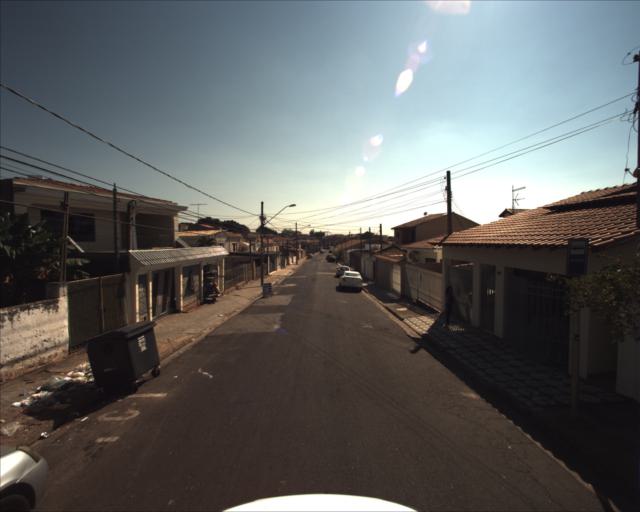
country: BR
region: Sao Paulo
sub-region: Sorocaba
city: Sorocaba
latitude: -23.4828
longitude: -47.4484
